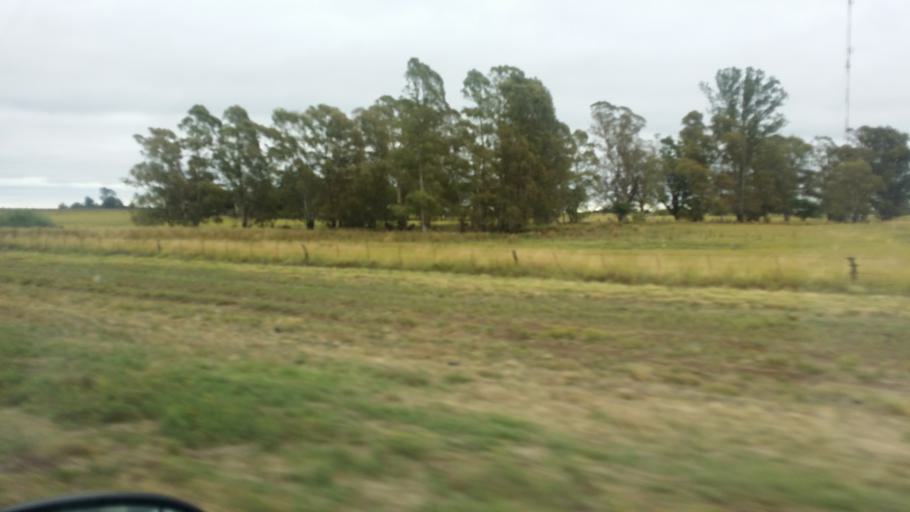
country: AR
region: La Pampa
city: Uriburu
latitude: -36.5155
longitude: -63.7437
